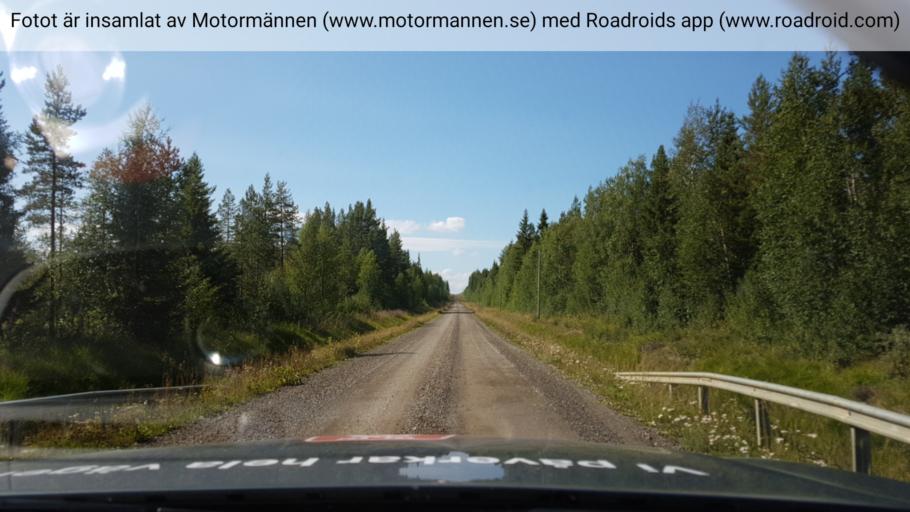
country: SE
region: Vaesterbotten
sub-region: Dorotea Kommun
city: Dorotea
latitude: 64.0912
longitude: 16.5179
